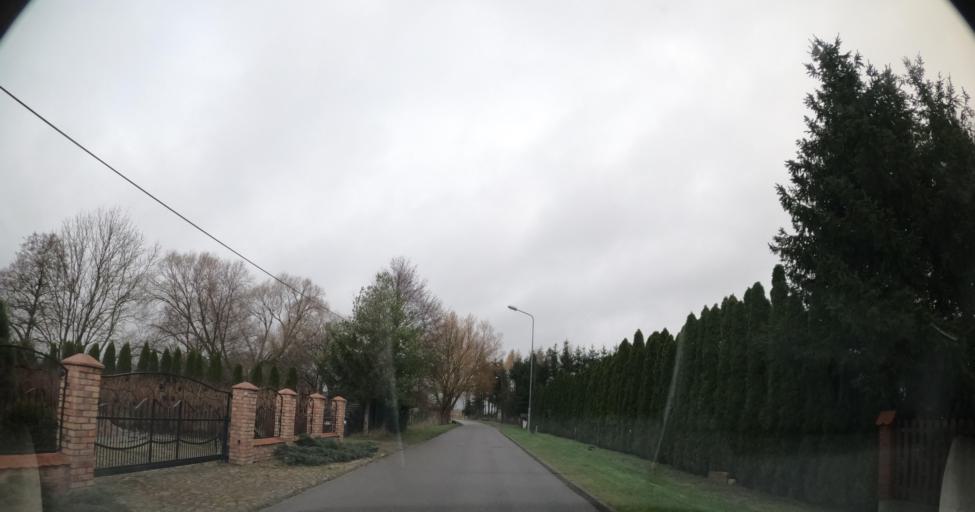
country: PL
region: West Pomeranian Voivodeship
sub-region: Powiat drawski
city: Drawsko Pomorskie
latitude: 53.5345
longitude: 15.8248
